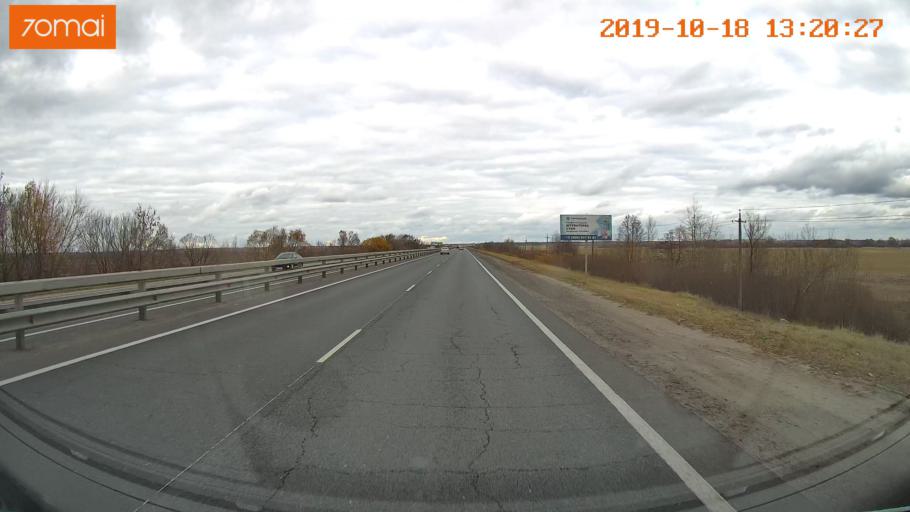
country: RU
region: Rjazan
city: Polyany
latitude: 54.6812
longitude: 39.8312
